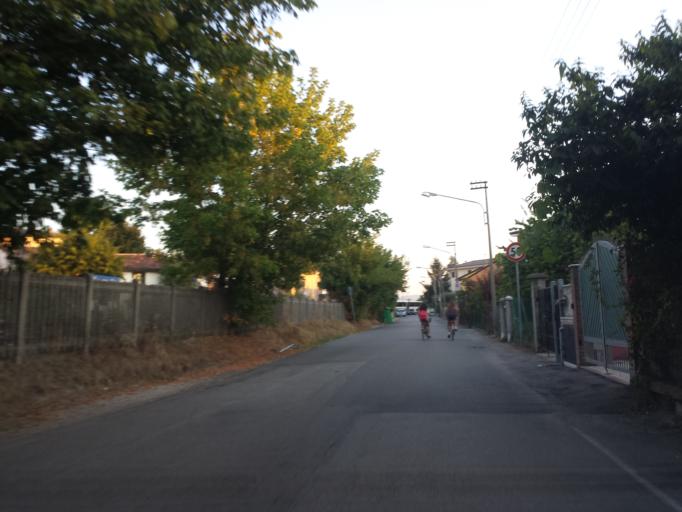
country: IT
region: Veneto
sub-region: Provincia di Vicenza
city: Vicenza
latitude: 45.5669
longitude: 11.5679
